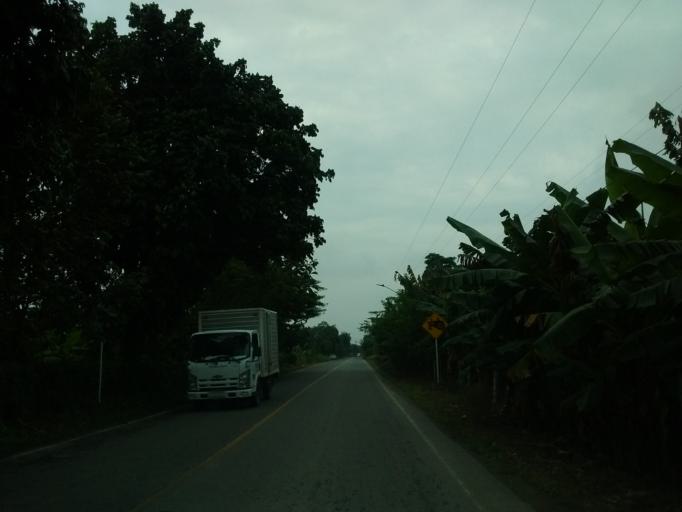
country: CO
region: Cauca
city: Padilla
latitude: 3.2298
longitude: -76.3297
